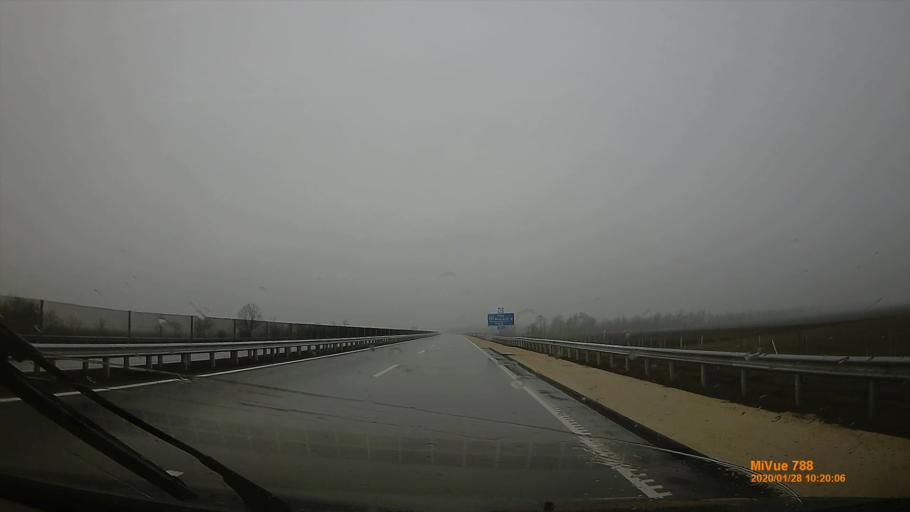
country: HU
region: Pest
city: Pilis
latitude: 47.3041
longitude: 19.5642
